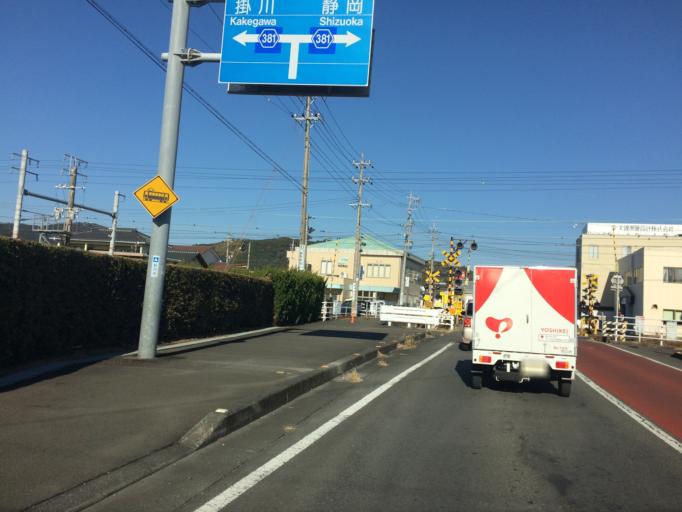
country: JP
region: Shizuoka
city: Shimada
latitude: 34.8376
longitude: 138.2099
